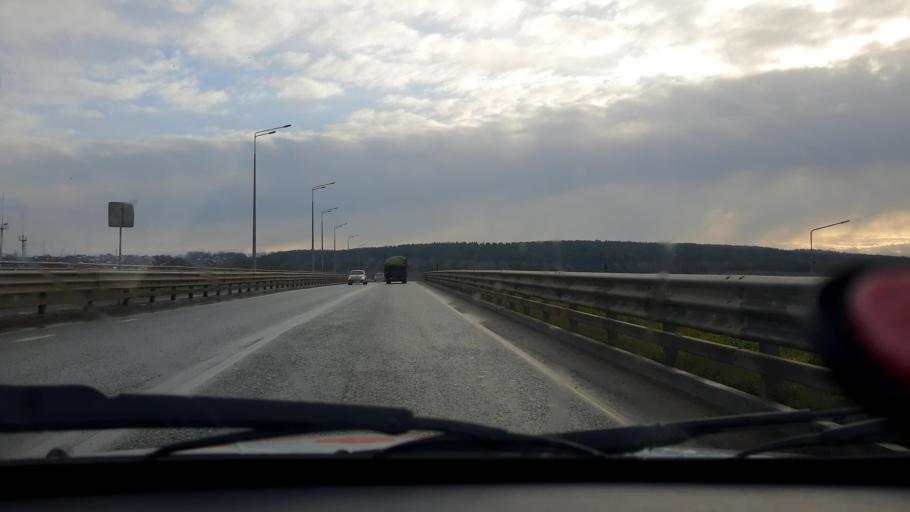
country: RU
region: Bashkortostan
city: Ufa
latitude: 54.8284
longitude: 56.1222
